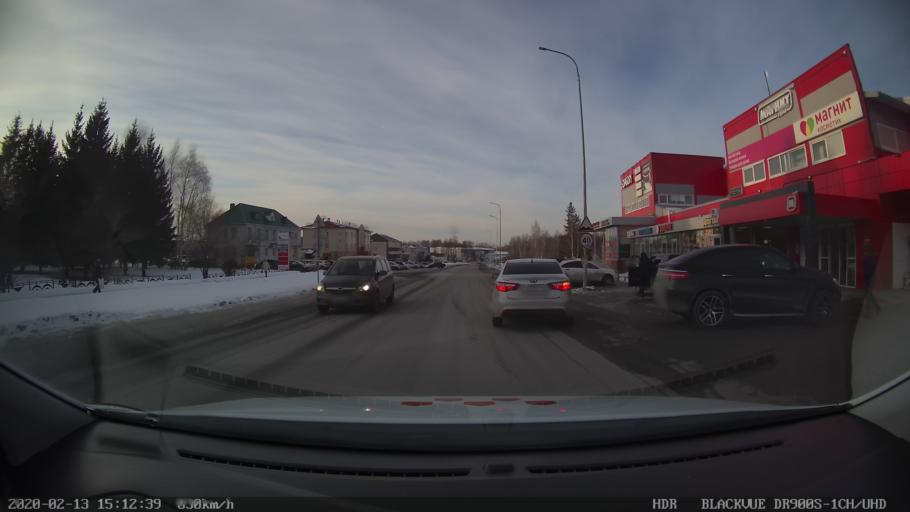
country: RU
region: Tatarstan
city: Vysokaya Gora
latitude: 55.9205
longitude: 49.3094
